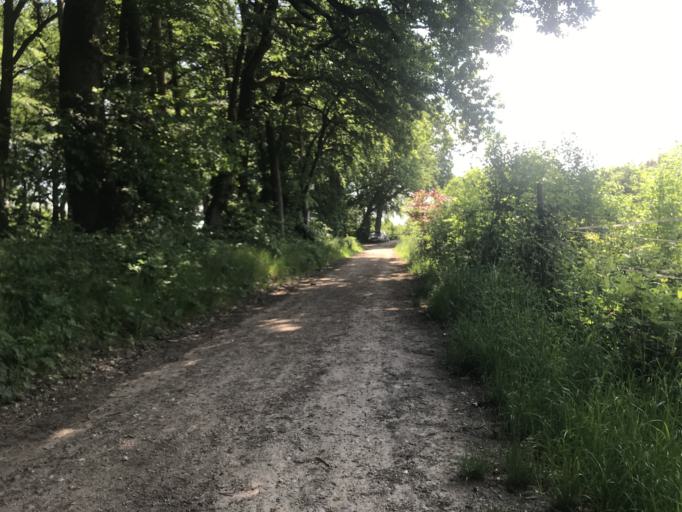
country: DE
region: Hesse
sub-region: Regierungsbezirk Darmstadt
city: Walluf
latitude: 50.0721
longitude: 8.1563
